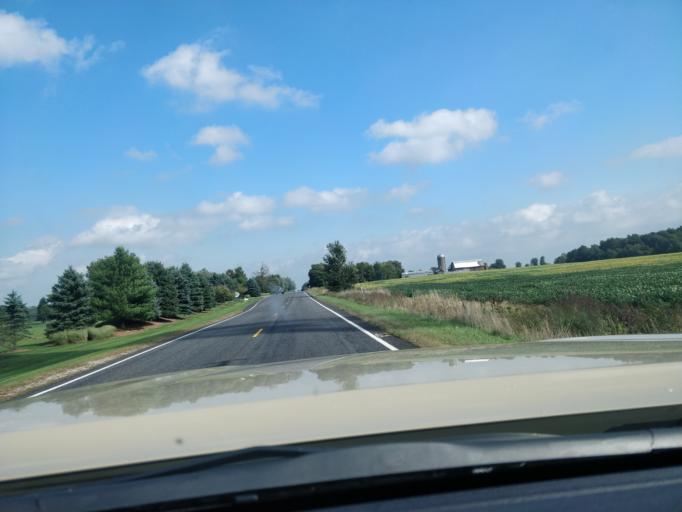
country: US
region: Michigan
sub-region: Ionia County
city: Saranac
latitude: 42.8861
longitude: -85.1538
